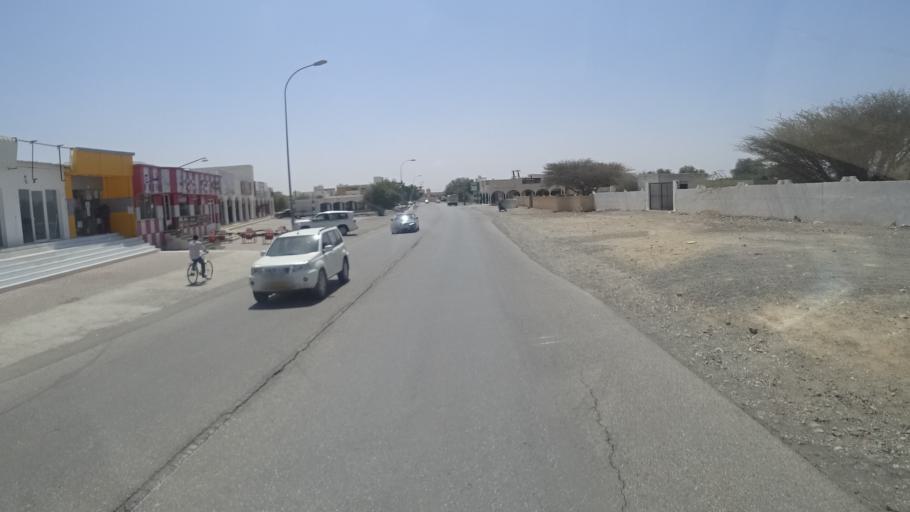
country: OM
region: Ash Sharqiyah
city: Ibra'
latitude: 22.6904
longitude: 58.5436
